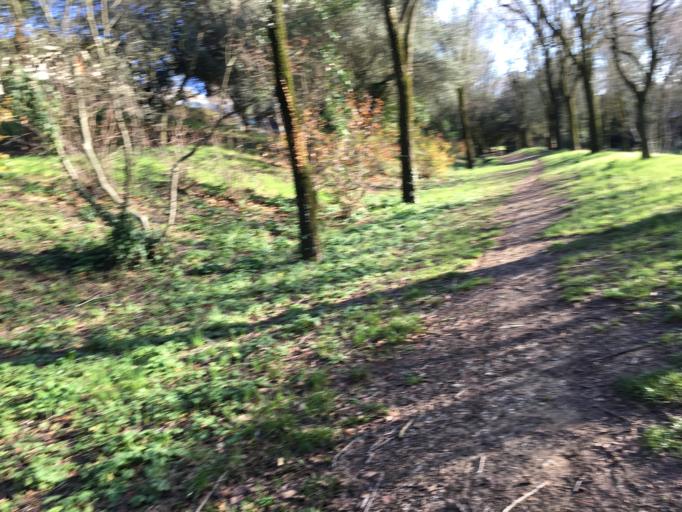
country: IT
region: Umbria
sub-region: Provincia di Perugia
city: Perugia
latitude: 43.1045
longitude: 12.3807
